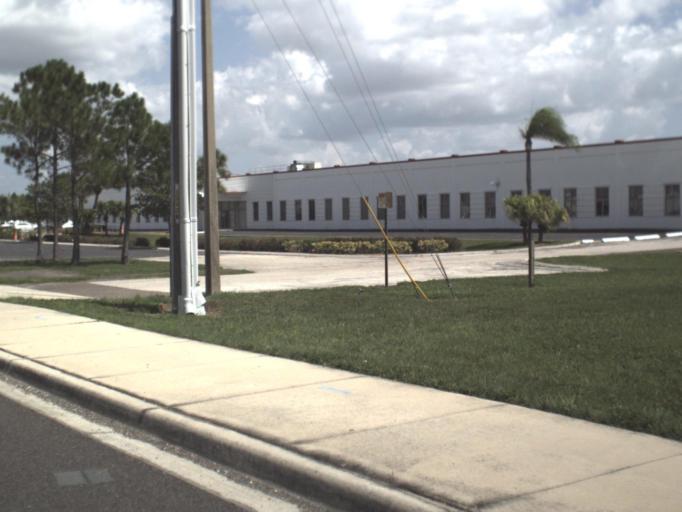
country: US
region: Florida
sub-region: Pinellas County
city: South Highpoint
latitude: 27.8935
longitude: -82.7261
